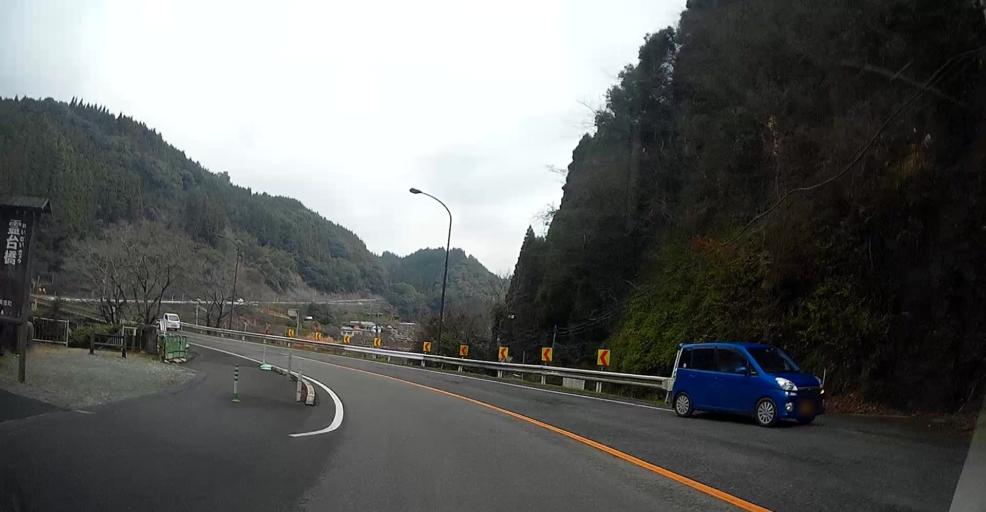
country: JP
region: Kumamoto
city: Matsubase
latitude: 32.6286
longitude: 130.8887
